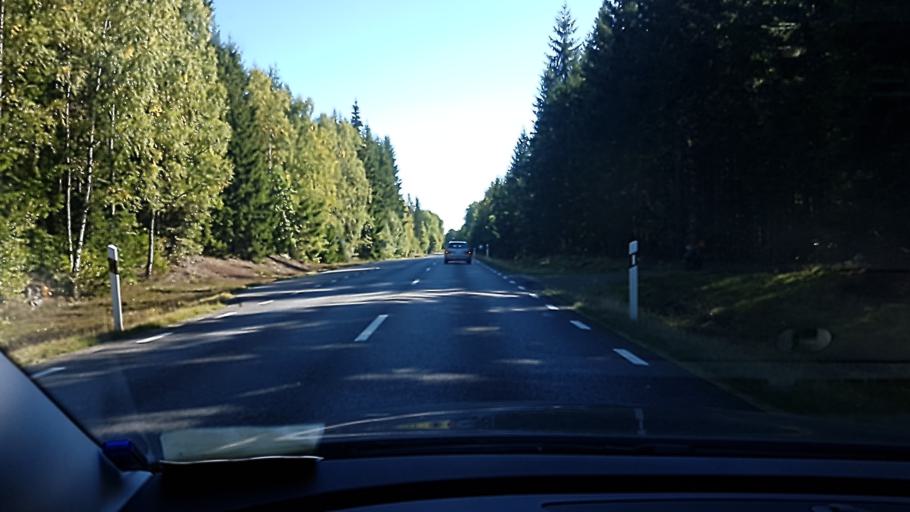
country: SE
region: Kalmar
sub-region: Emmaboda Kommun
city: Emmaboda
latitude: 56.7330
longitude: 15.4539
